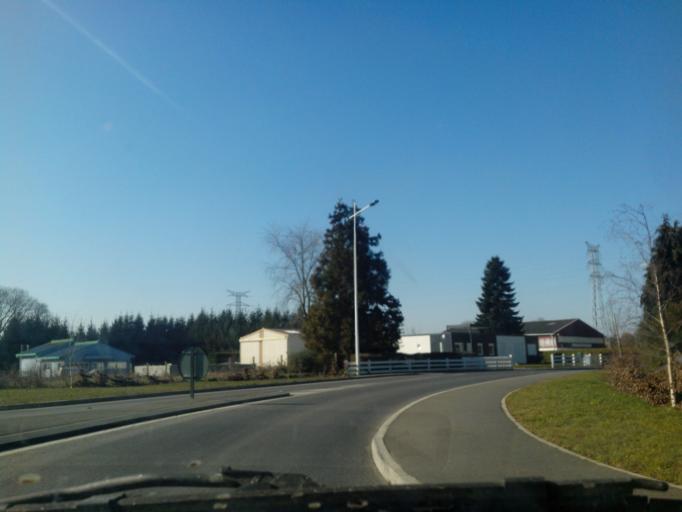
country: FR
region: Brittany
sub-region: Departement des Cotes-d'Armor
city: Loudeac
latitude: 48.1661
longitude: -2.7489
